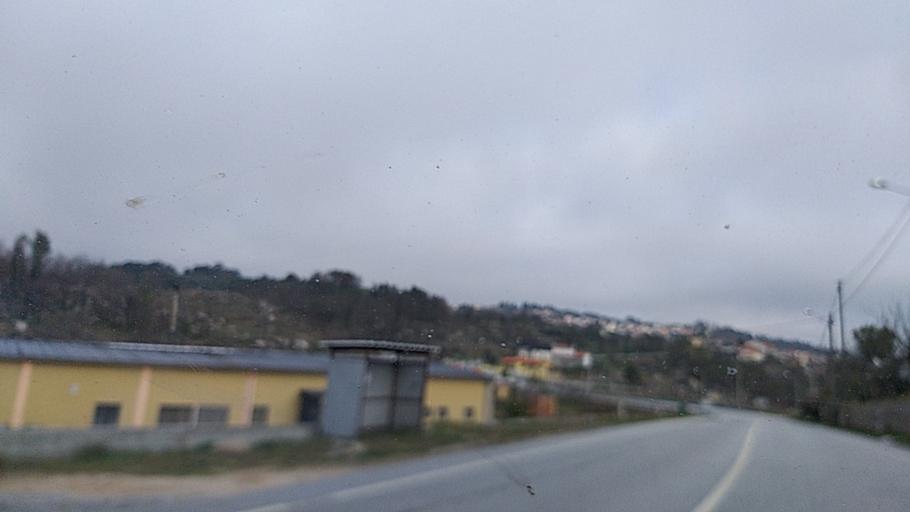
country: PT
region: Guarda
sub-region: Fornos de Algodres
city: Fornos de Algodres
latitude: 40.6755
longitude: -7.4716
